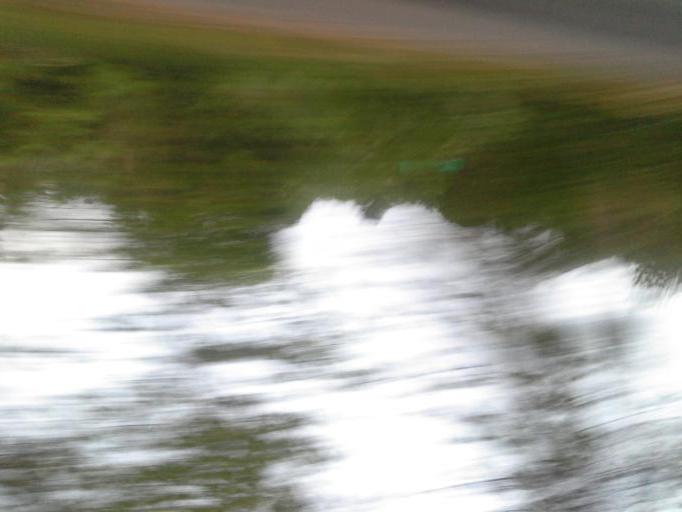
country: CO
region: Sucre
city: Los Palmitos
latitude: 9.3744
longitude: -75.2729
